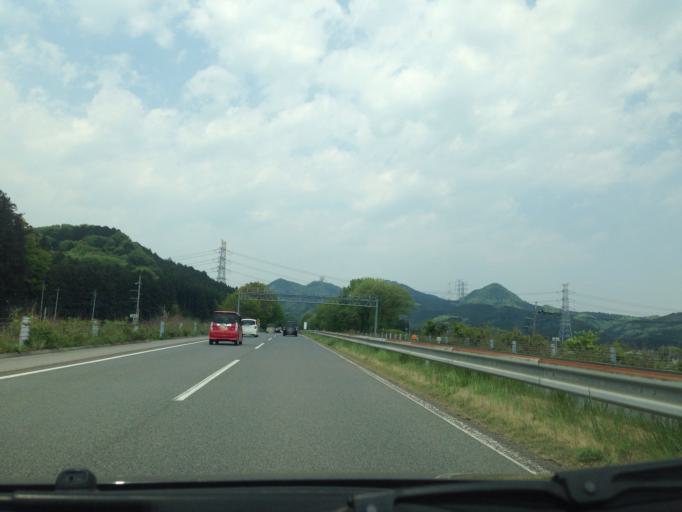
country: JP
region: Tochigi
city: Utsunomiya-shi
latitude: 36.6552
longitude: 139.8360
